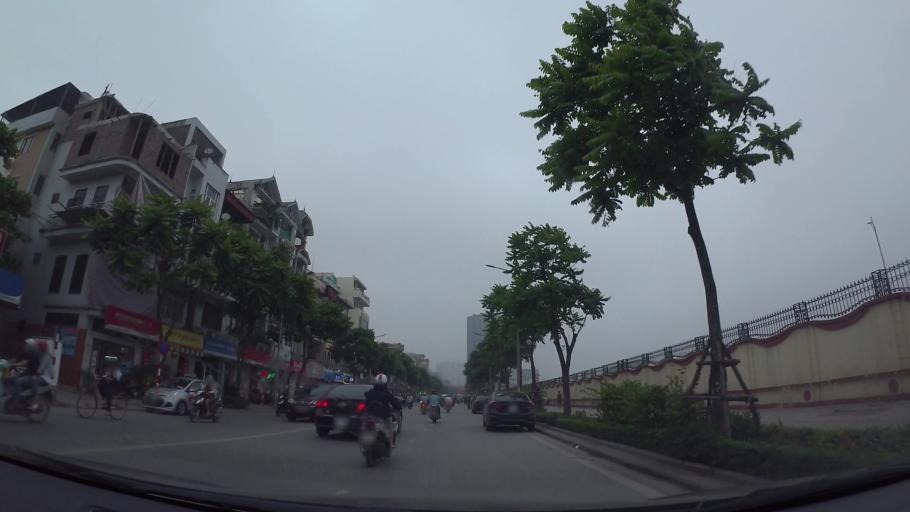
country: VN
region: Ha Noi
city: Dong Da
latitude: 20.9954
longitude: 105.8306
